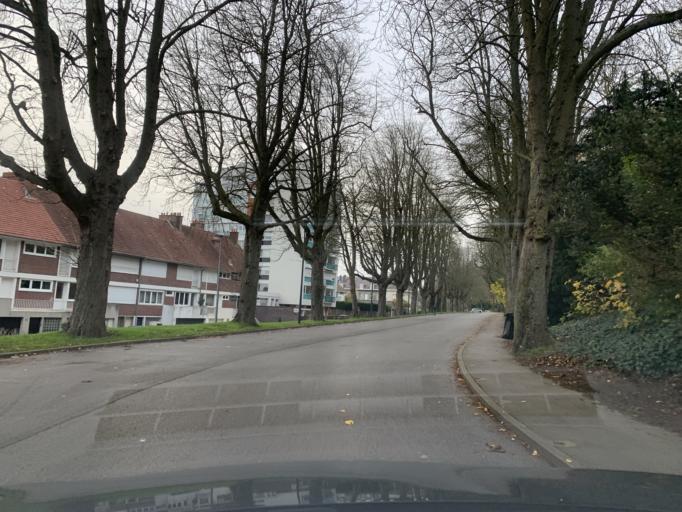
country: FR
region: Nord-Pas-de-Calais
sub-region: Departement du Nord
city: Cambrai
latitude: 50.1714
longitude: 3.2370
